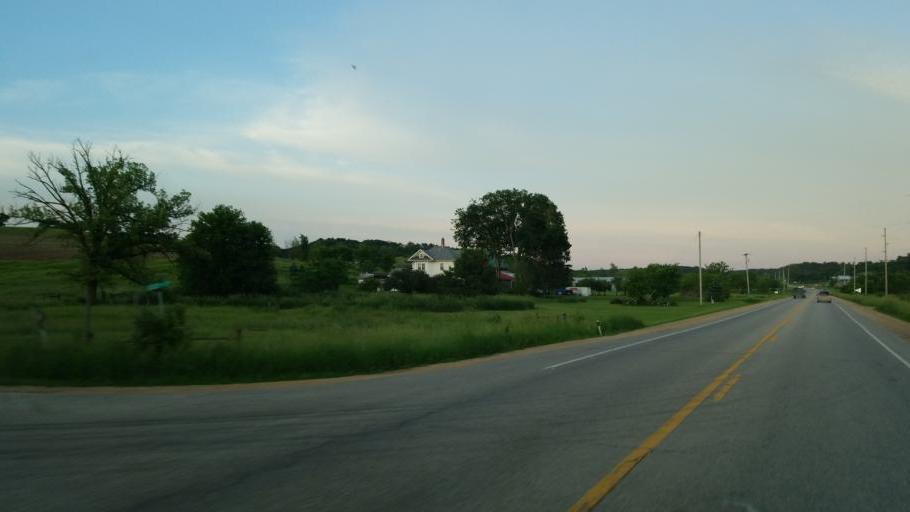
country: US
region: Wisconsin
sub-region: Monroe County
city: Tomah
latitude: 43.8315
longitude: -90.4681
